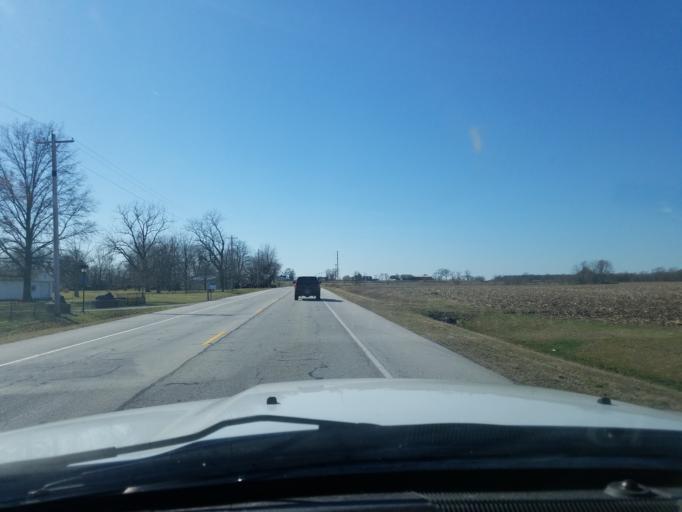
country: US
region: Indiana
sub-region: Shelby County
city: Shelbyville
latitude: 39.4957
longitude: -85.9038
